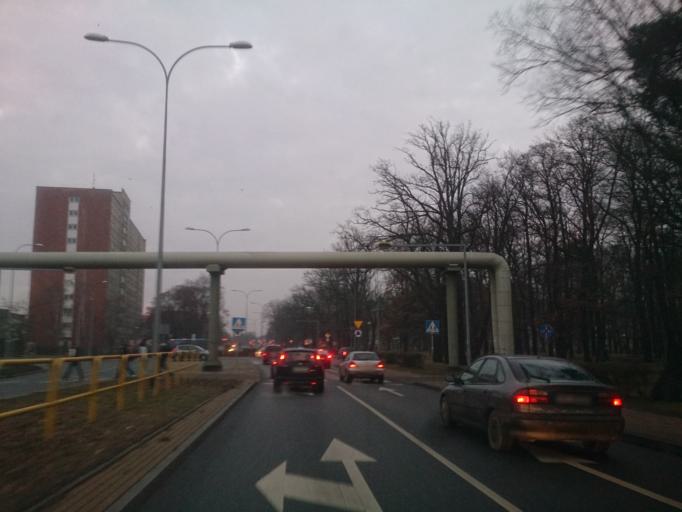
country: PL
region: Kujawsko-Pomorskie
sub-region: Grudziadz
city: Grudziadz
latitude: 53.4769
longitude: 18.7566
